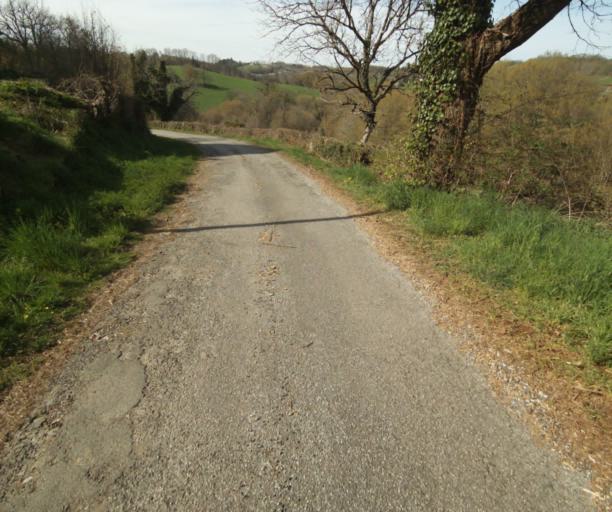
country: FR
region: Limousin
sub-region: Departement de la Correze
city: Naves
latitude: 45.3532
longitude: 1.7605
